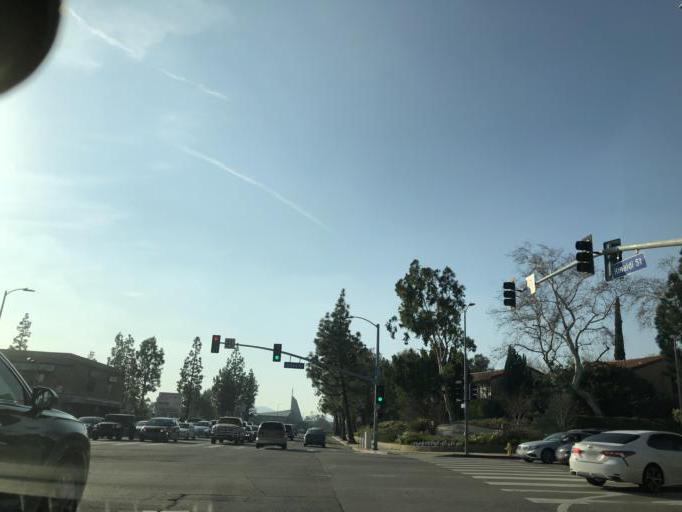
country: US
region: California
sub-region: Los Angeles County
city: Chatsworth
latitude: 34.2748
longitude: -118.5563
